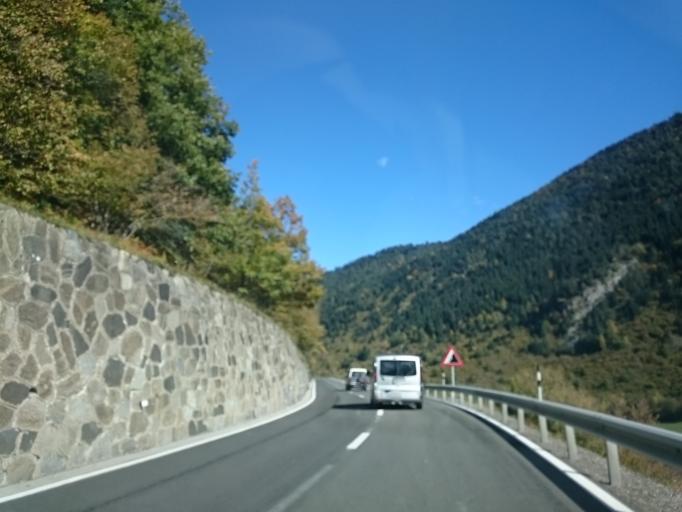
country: ES
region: Catalonia
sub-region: Provincia de Lleida
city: Vielha
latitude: 42.6779
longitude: 0.7850
